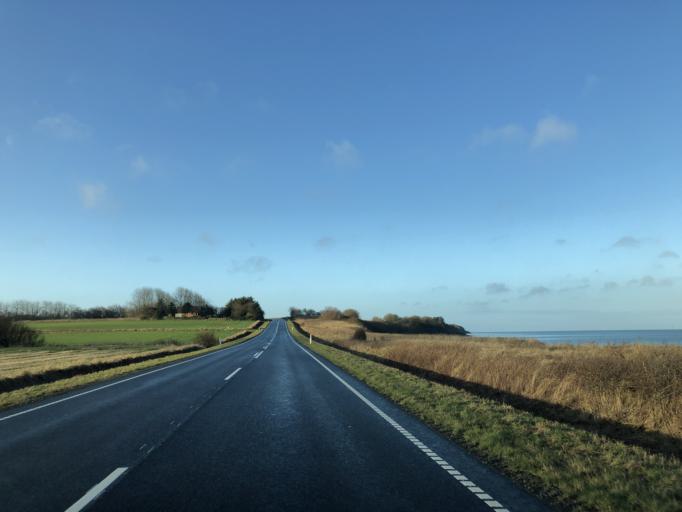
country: DK
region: Central Jutland
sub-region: Struer Kommune
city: Struer
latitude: 56.5585
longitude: 8.4623
